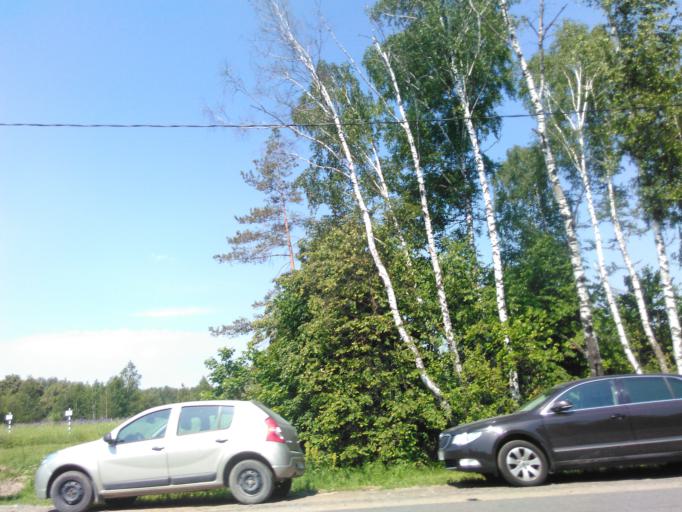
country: RU
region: Moskovskaya
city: Vishnyakovskiye Dachi
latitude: 55.8141
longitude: 38.1178
